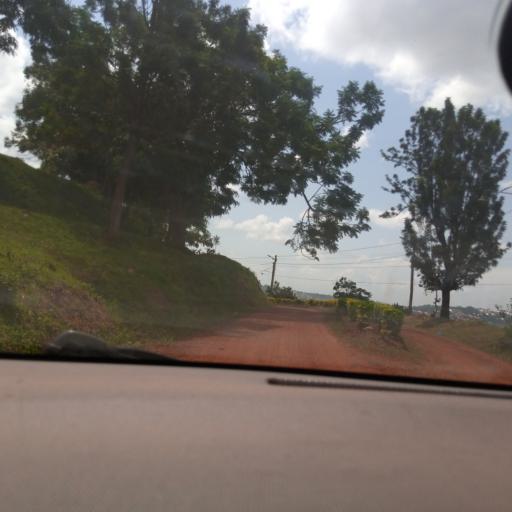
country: UG
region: Central Region
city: Masaka
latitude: -0.3235
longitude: 31.7422
